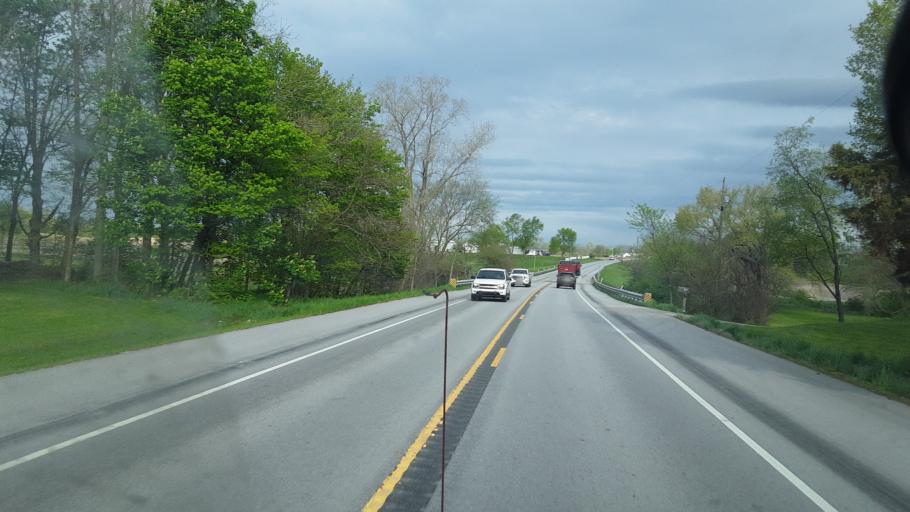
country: US
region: Indiana
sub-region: Whitley County
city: Churubusco
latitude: 41.2578
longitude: -85.3704
